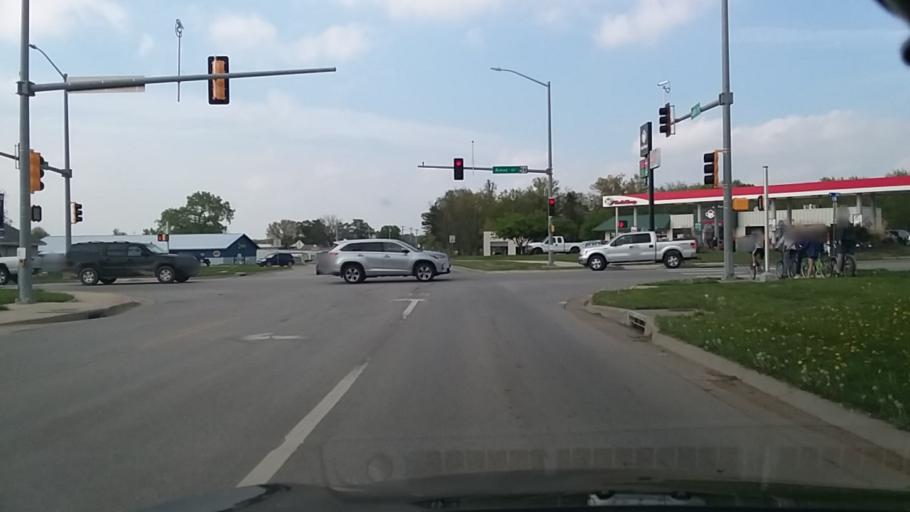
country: US
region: Kansas
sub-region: Douglas County
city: Baldwin City
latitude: 38.7819
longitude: -95.1862
